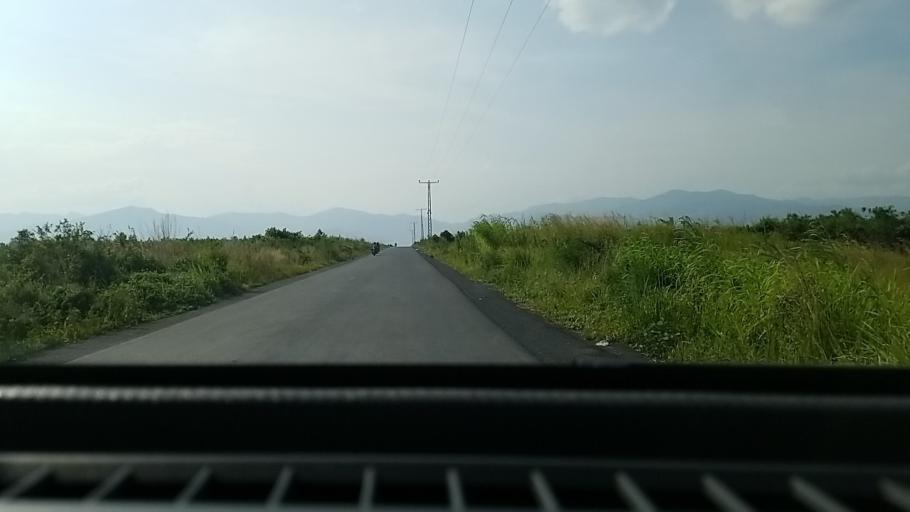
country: CD
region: Nord Kivu
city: Sake
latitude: -1.5957
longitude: 29.1046
